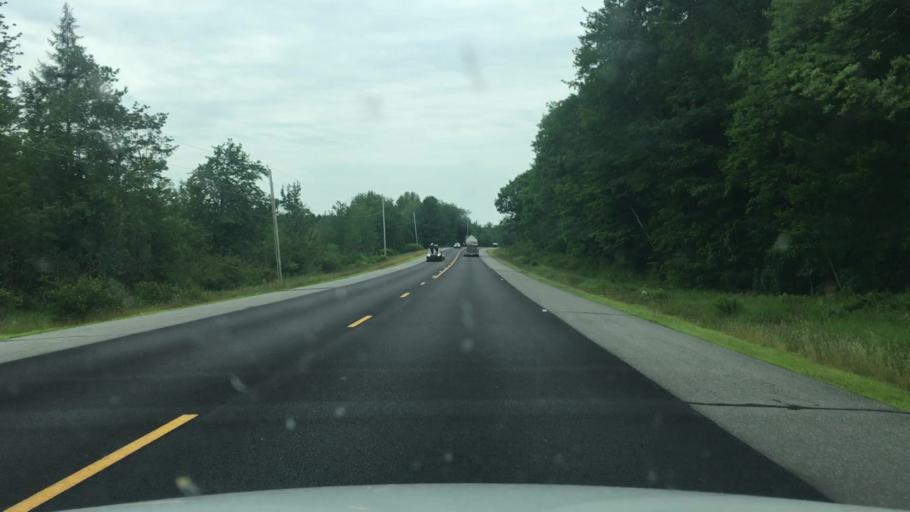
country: US
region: Maine
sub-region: Knox County
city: Washington
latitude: 44.3749
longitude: -69.3743
